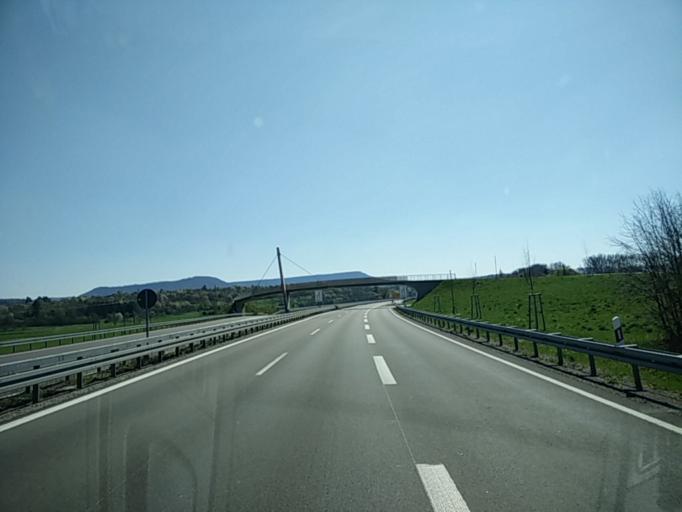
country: DE
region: Baden-Wuerttemberg
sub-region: Tuebingen Region
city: Dusslingen
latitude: 48.4411
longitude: 9.0576
